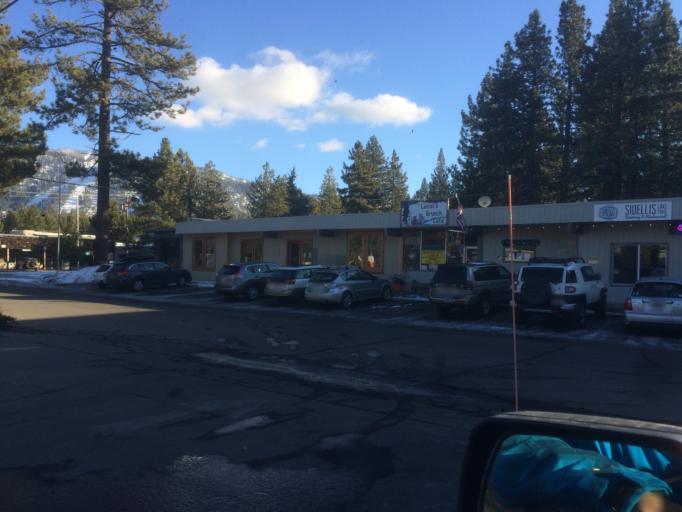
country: US
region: California
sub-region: El Dorado County
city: South Lake Tahoe
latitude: 38.9449
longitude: -119.9696
